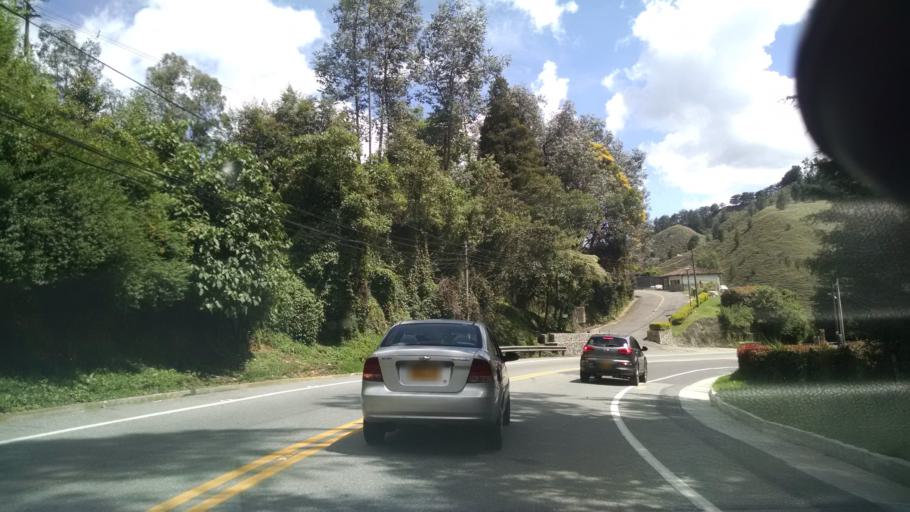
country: CO
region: Antioquia
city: El Retiro
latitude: 6.1334
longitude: -75.5071
